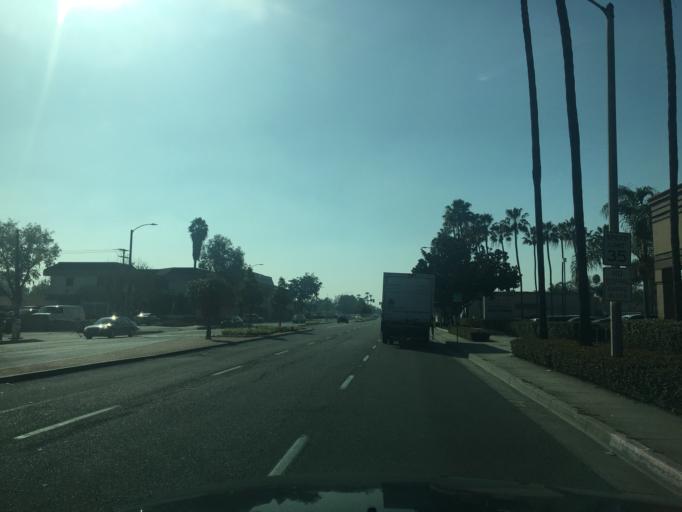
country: US
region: California
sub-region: Orange County
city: Tustin
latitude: 33.7418
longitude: -117.8187
